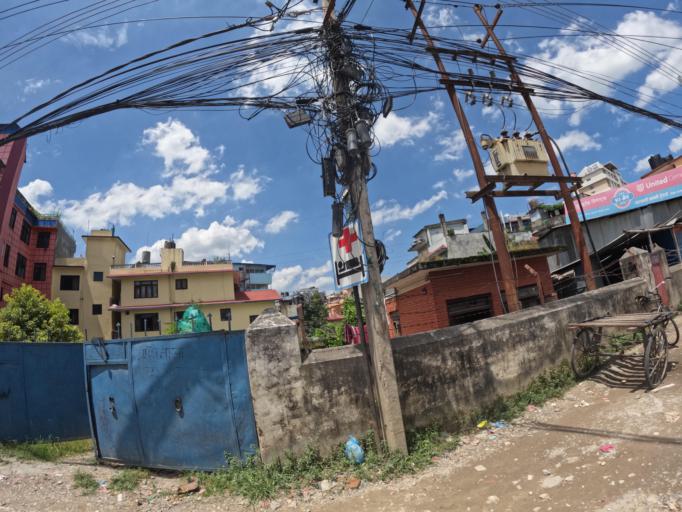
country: NP
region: Central Region
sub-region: Bagmati Zone
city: Kathmandu
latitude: 27.7511
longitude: 85.3256
